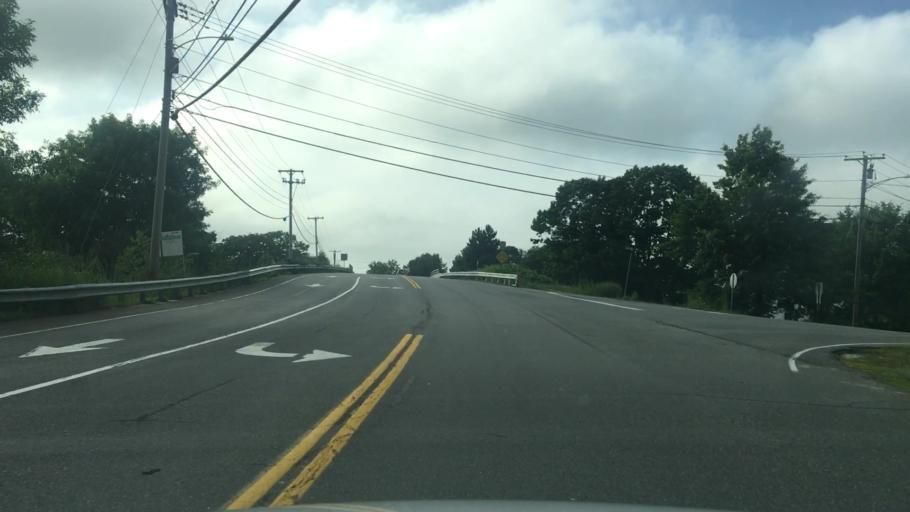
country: US
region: Maine
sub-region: Cumberland County
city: Scarborough
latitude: 43.5773
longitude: -70.3217
